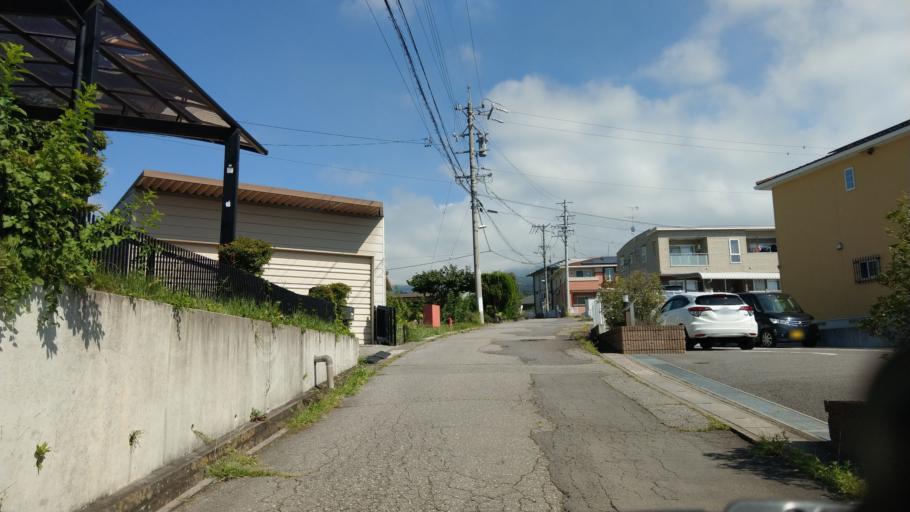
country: JP
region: Nagano
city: Komoro
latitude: 36.3350
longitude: 138.4104
